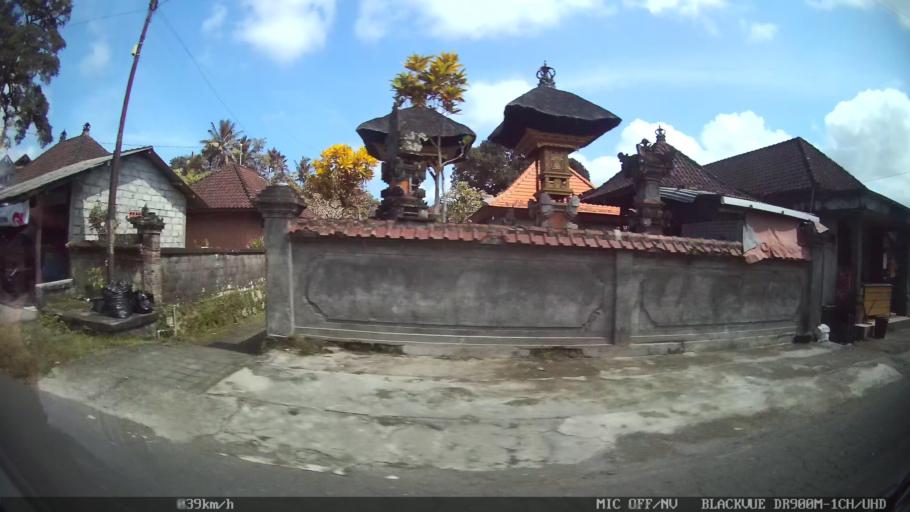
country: ID
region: Bali
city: Banjar Apuan Kaja
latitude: -8.5147
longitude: 115.3275
